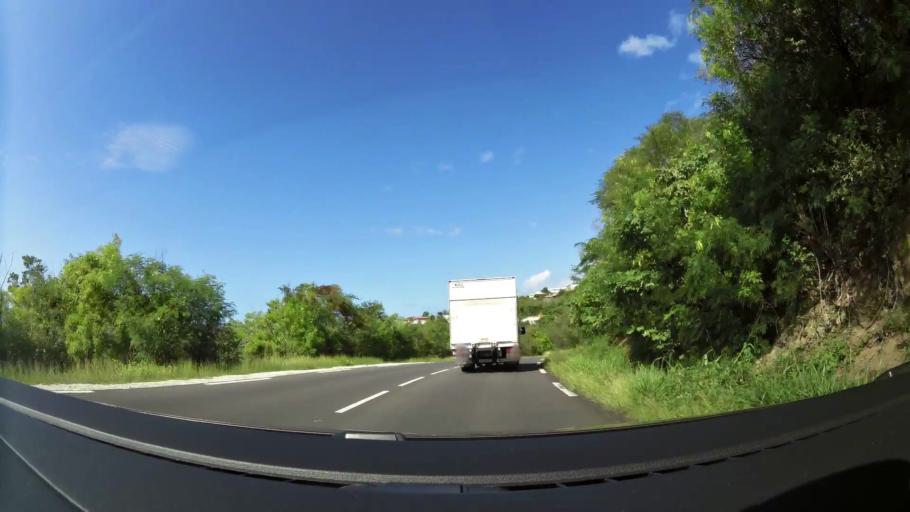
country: GP
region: Guadeloupe
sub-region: Guadeloupe
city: Bouillante
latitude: 16.1072
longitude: -61.7727
